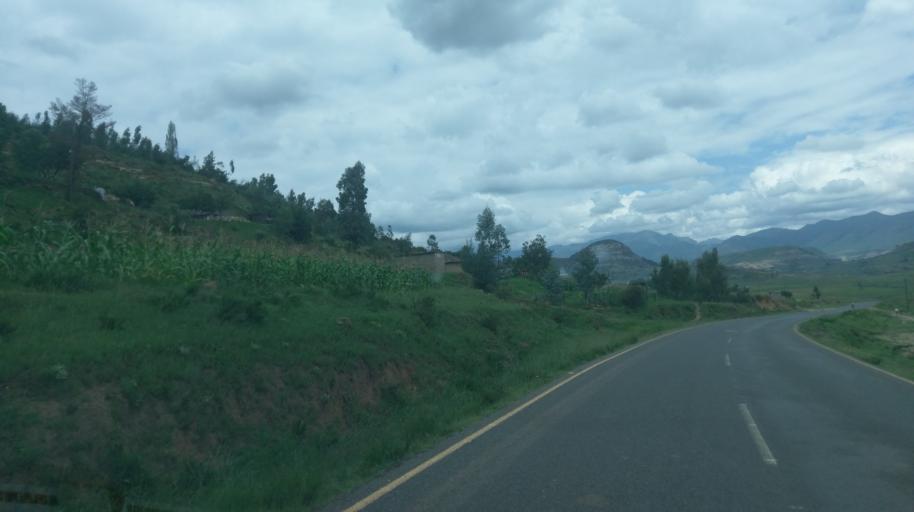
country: LS
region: Leribe
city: Leribe
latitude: -28.9654
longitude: 28.1727
